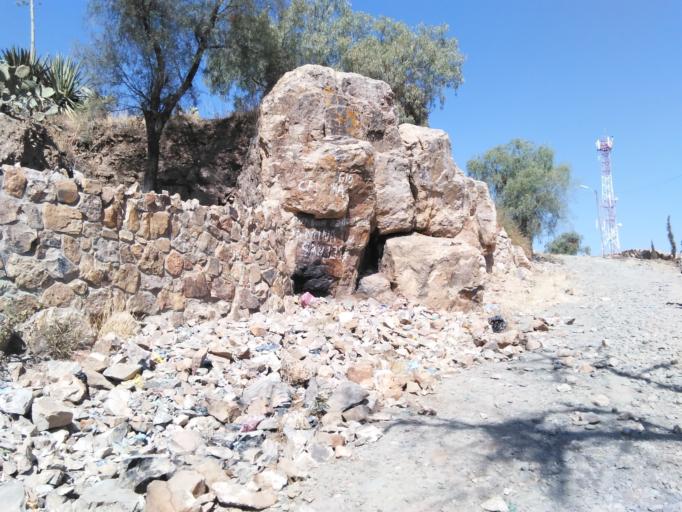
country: BO
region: Cochabamba
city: Sipe Sipe
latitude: -17.4226
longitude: -66.2844
